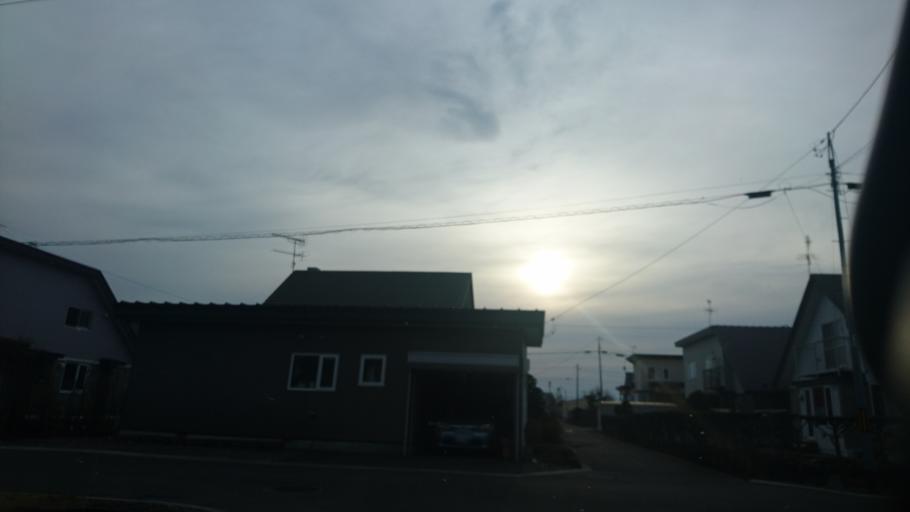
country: JP
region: Hokkaido
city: Otofuke
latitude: 43.0008
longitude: 143.1942
